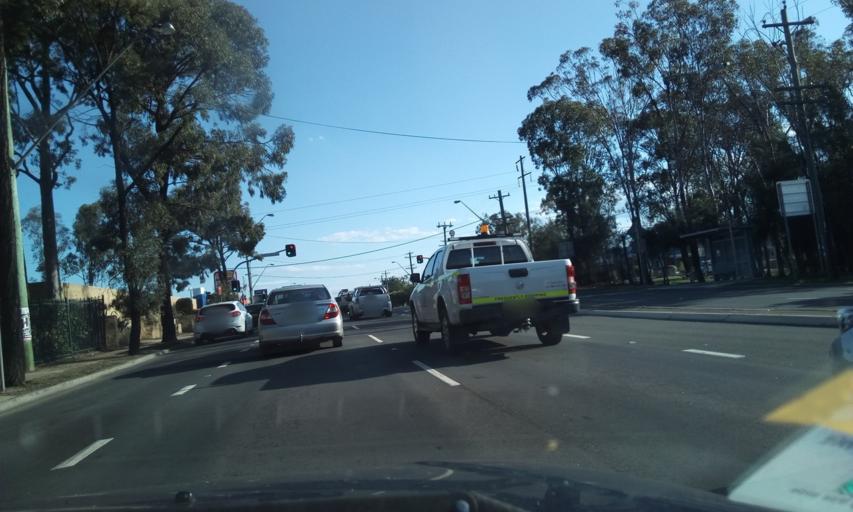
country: AU
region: New South Wales
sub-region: Penrith Municipality
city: Cambridge Park
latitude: -33.7536
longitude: 150.7130
